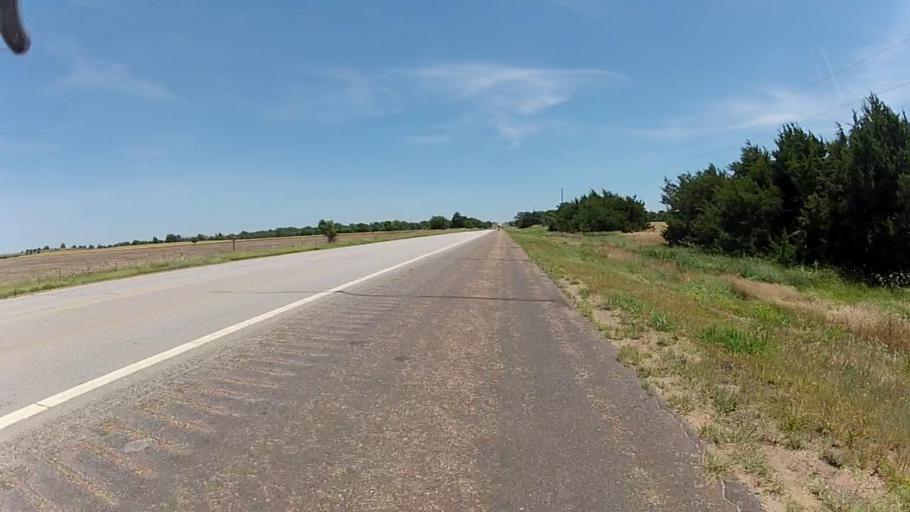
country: US
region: Kansas
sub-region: Barber County
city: Medicine Lodge
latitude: 37.2533
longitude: -98.3057
